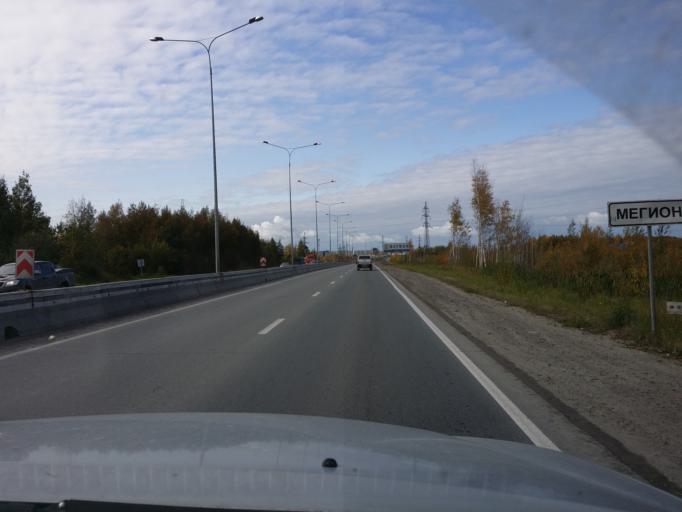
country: RU
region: Khanty-Mansiyskiy Avtonomnyy Okrug
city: Megion
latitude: 61.0499
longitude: 76.1355
